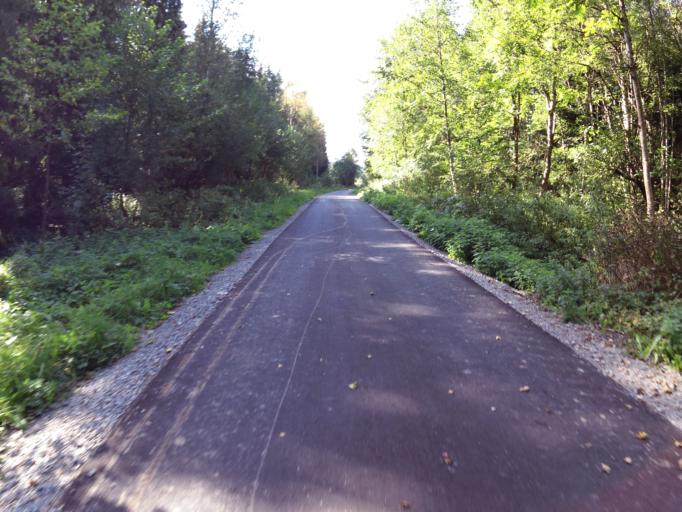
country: DE
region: Baden-Wuerttemberg
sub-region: Freiburg Region
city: Dauchingen
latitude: 48.0738
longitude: 8.5795
